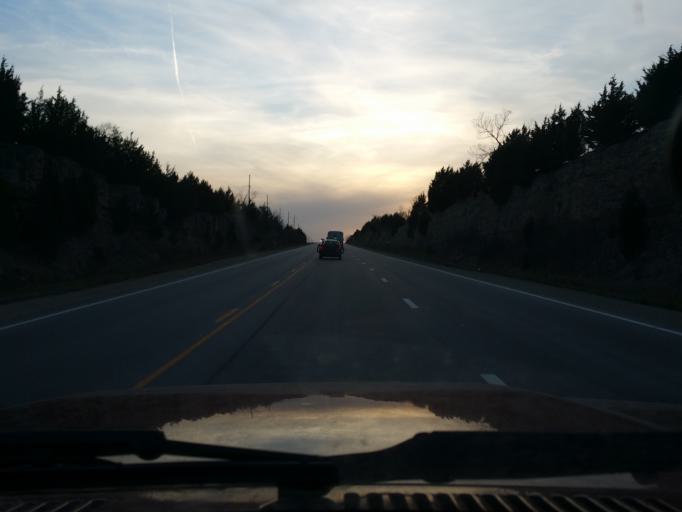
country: US
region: Kansas
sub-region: Riley County
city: Manhattan
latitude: 39.2517
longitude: -96.6442
